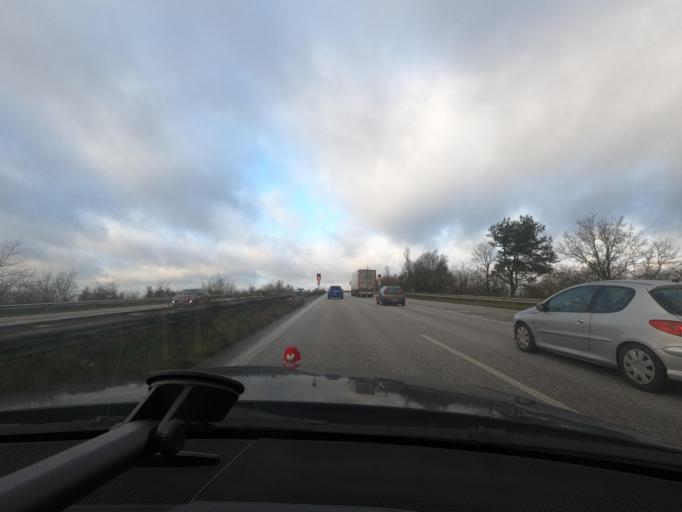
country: DE
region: Schleswig-Holstein
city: Borgstedt
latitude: 54.3266
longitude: 9.7333
